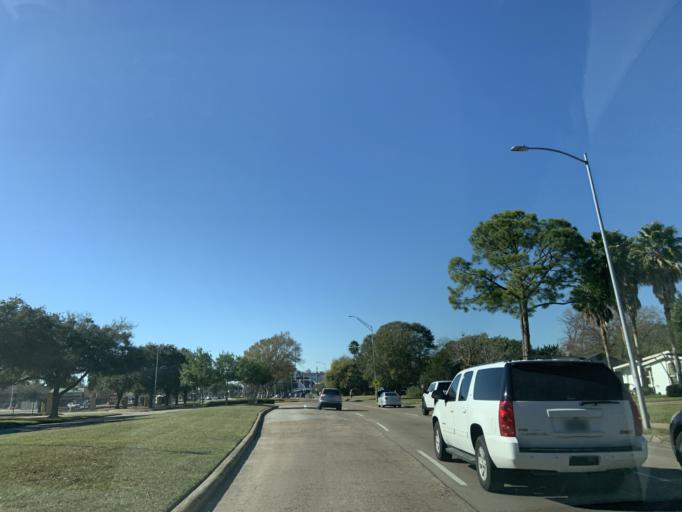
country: US
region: Texas
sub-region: Harris County
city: Bellaire
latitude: 29.6921
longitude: -95.5076
